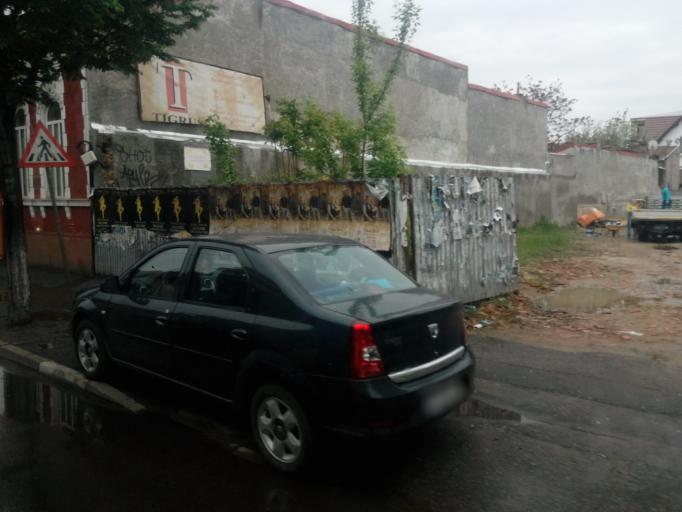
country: RO
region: Bucuresti
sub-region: Municipiul Bucuresti
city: Bucharest
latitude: 44.4421
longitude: 26.1261
